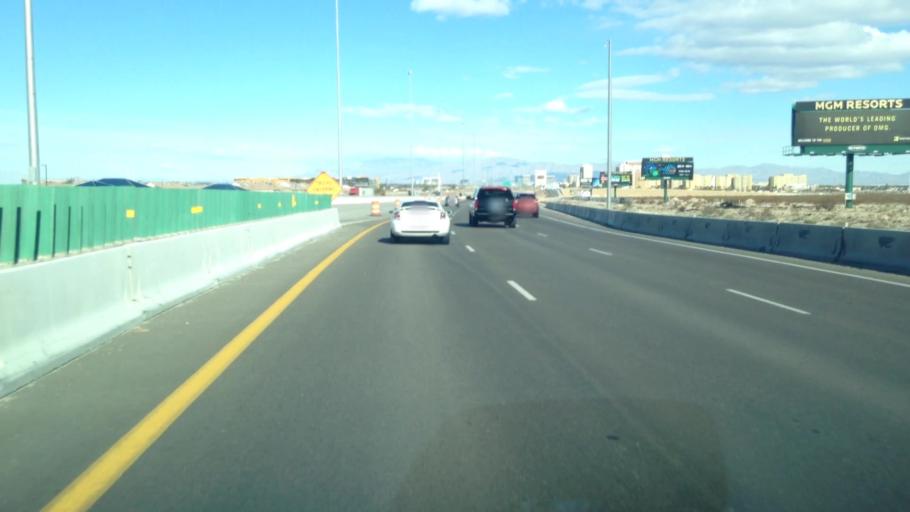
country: US
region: Nevada
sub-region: Clark County
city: Enterprise
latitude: 35.9894
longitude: -115.1806
